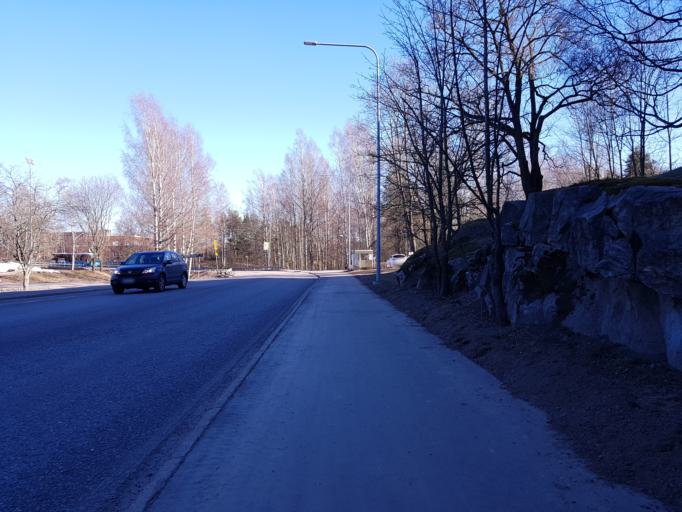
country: FI
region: Uusimaa
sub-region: Helsinki
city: Vantaa
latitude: 60.2307
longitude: 25.0048
